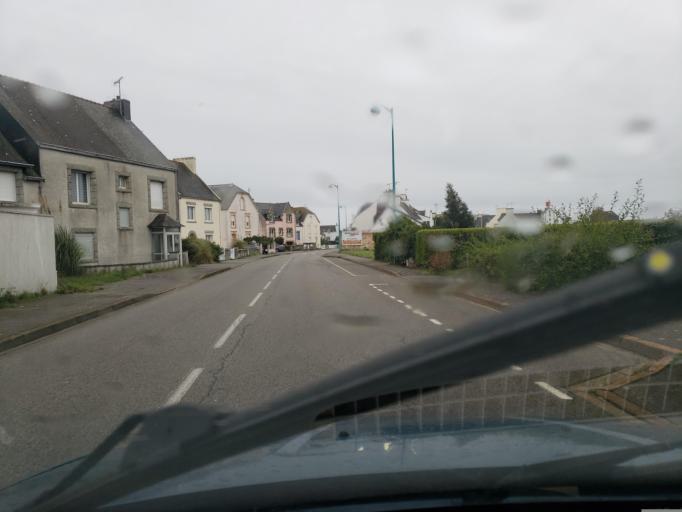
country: FR
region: Brittany
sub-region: Departement du Finistere
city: Guilvinec
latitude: 47.7977
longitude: -4.2680
